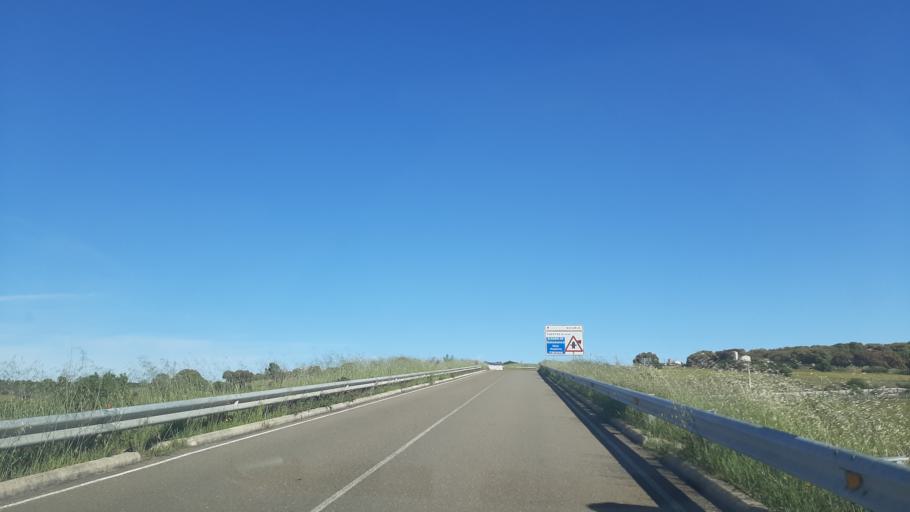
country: ES
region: Castille and Leon
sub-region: Provincia de Salamanca
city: Guijuelo
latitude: 40.5400
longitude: -5.6602
